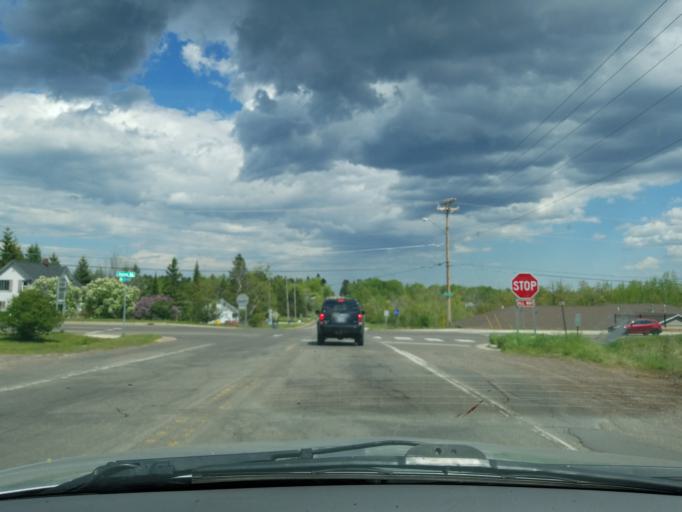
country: US
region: Minnesota
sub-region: Saint Louis County
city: Proctor
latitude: 46.7785
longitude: -92.1752
